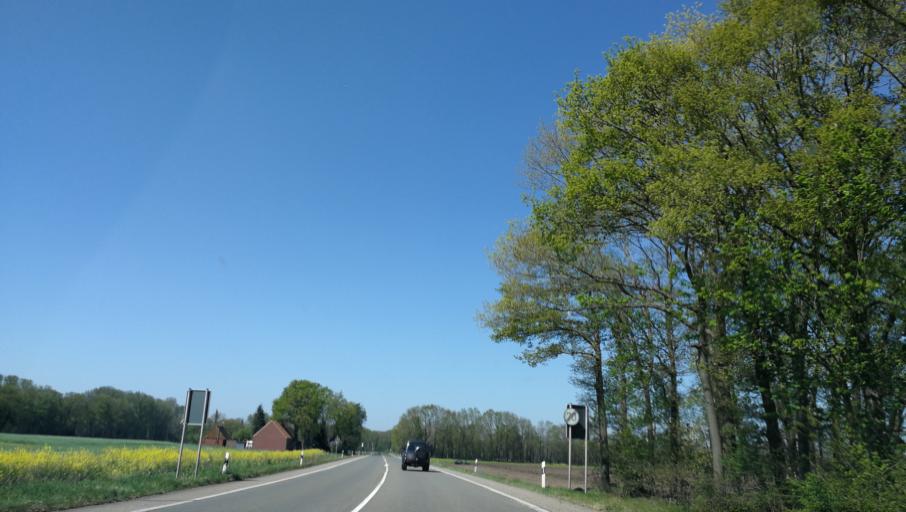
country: DE
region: North Rhine-Westphalia
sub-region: Regierungsbezirk Munster
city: Steinfurt
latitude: 52.1715
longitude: 7.3448
